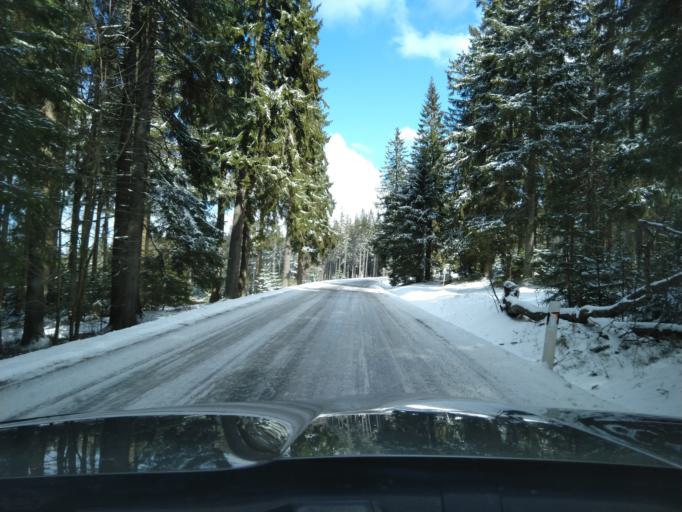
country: CZ
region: Jihocesky
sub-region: Okres Prachatice
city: Borova Lada
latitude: 49.0411
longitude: 13.6067
